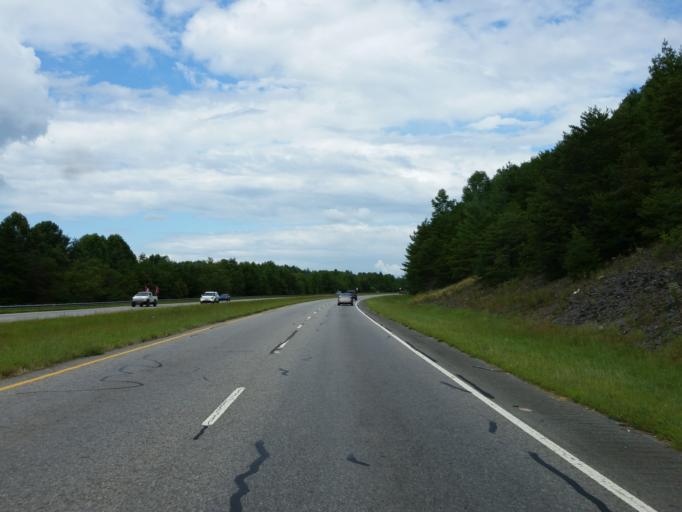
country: US
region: Georgia
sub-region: Fannin County
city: Blue Ridge
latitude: 34.8848
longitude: -84.2918
